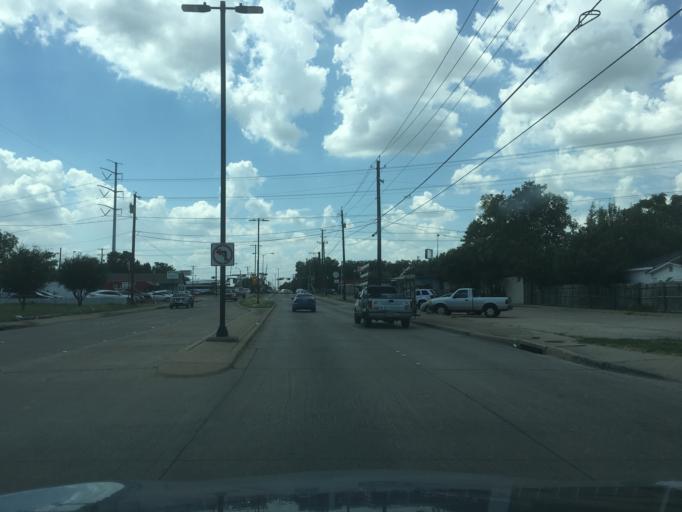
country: US
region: Texas
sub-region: Dallas County
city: Garland
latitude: 32.8790
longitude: -96.6581
